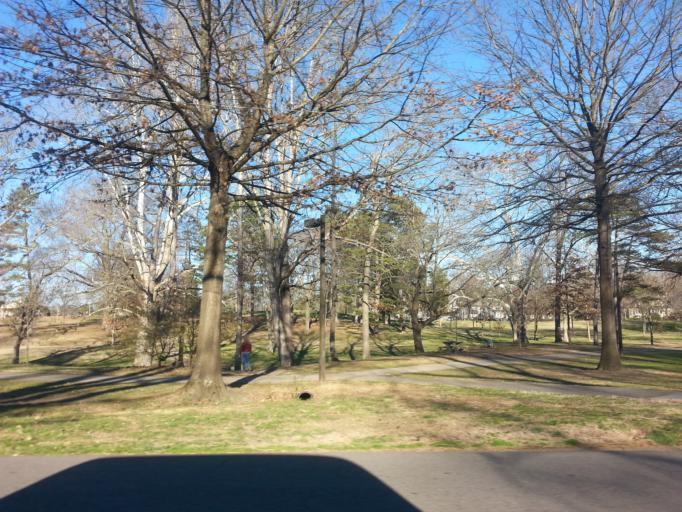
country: US
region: Tennessee
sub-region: Blount County
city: Alcoa
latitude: 35.7971
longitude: -83.9802
